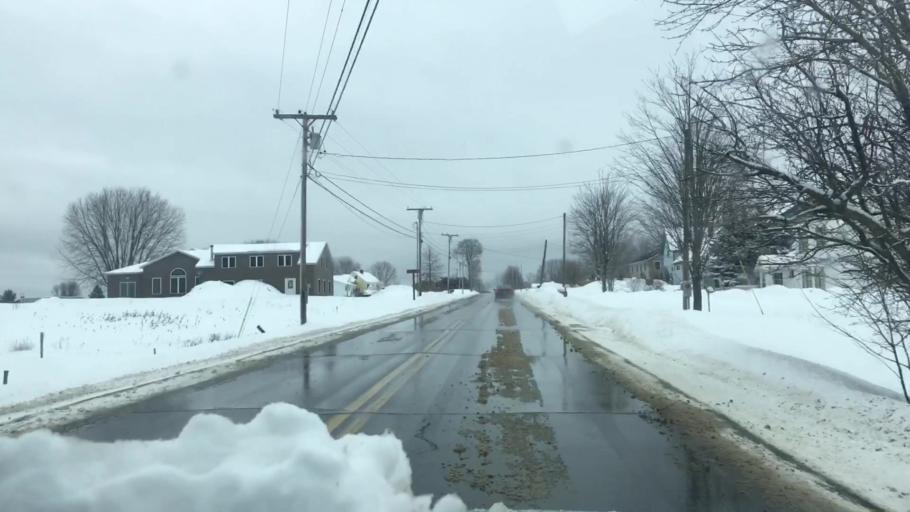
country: US
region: Maine
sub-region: Penobscot County
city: Charleston
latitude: 44.9956
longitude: -69.0494
